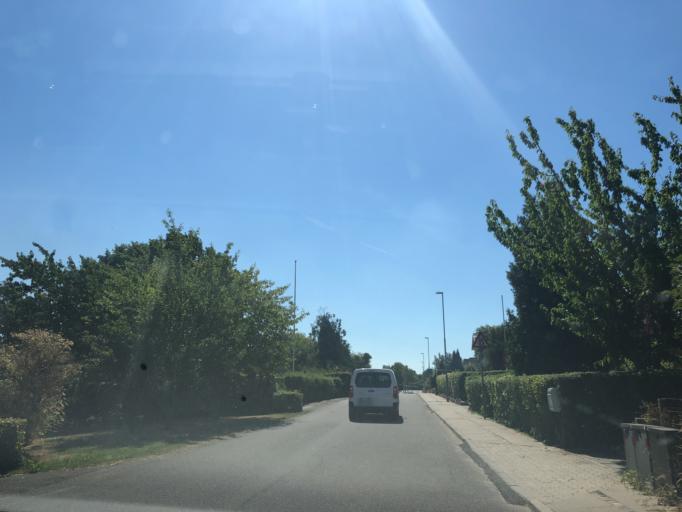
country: DK
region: Zealand
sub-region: Slagelse Kommune
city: Forlev
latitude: 55.3723
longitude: 11.2599
